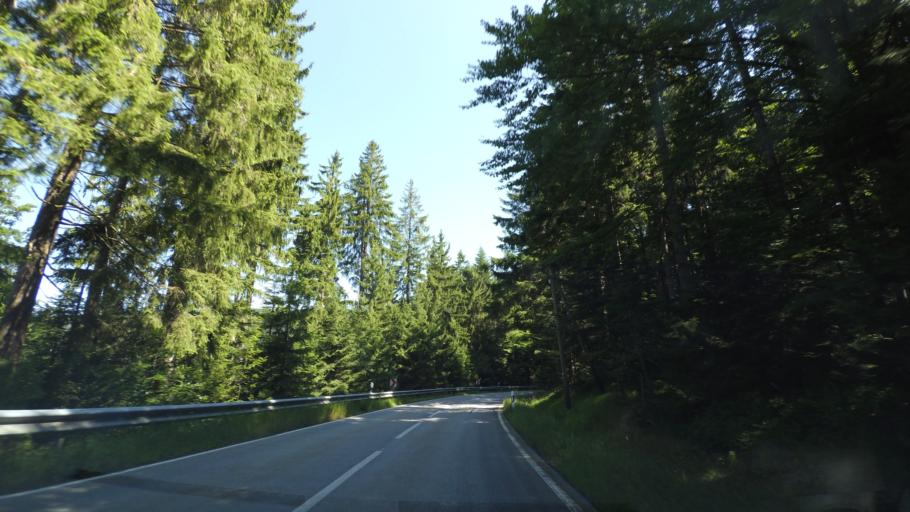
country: DE
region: Bavaria
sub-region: Upper Palatinate
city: Lohberg
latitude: 49.1663
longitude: 13.1396
